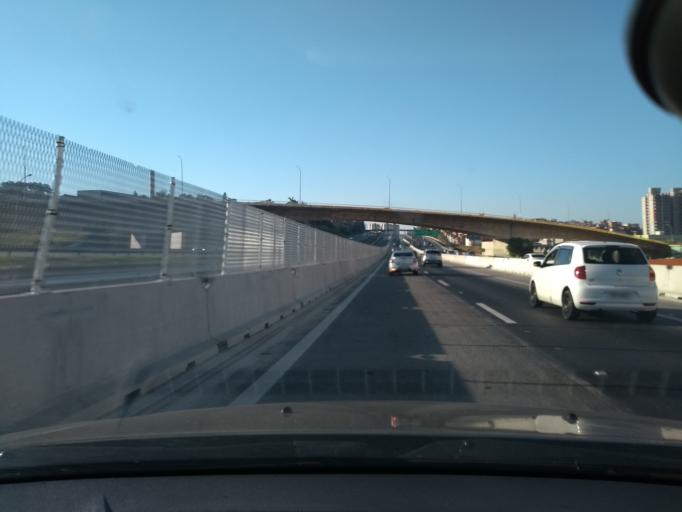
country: BR
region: Sao Paulo
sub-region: Sao Bernardo Do Campo
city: Sao Bernardo do Campo
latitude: -23.7097
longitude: -46.5610
